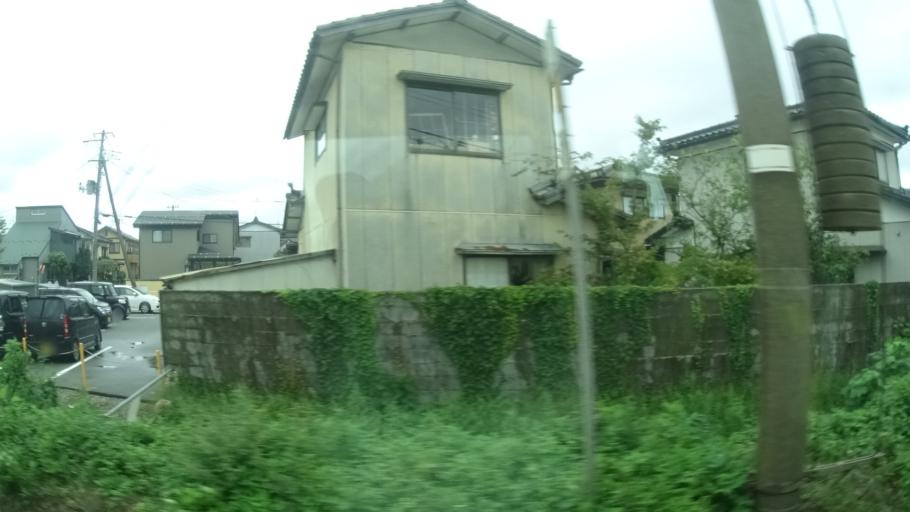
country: JP
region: Niigata
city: Murakami
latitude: 38.2151
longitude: 139.4634
